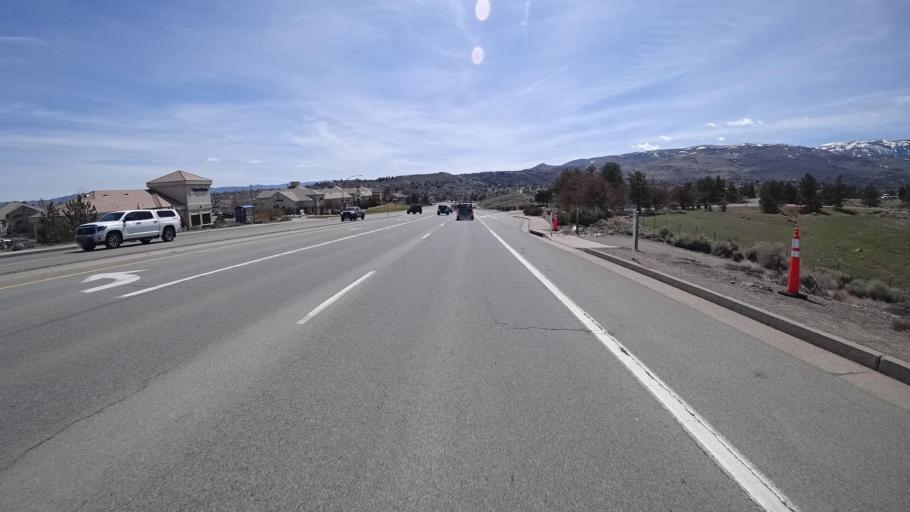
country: US
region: Nevada
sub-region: Washoe County
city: Reno
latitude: 39.5154
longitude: -119.8604
